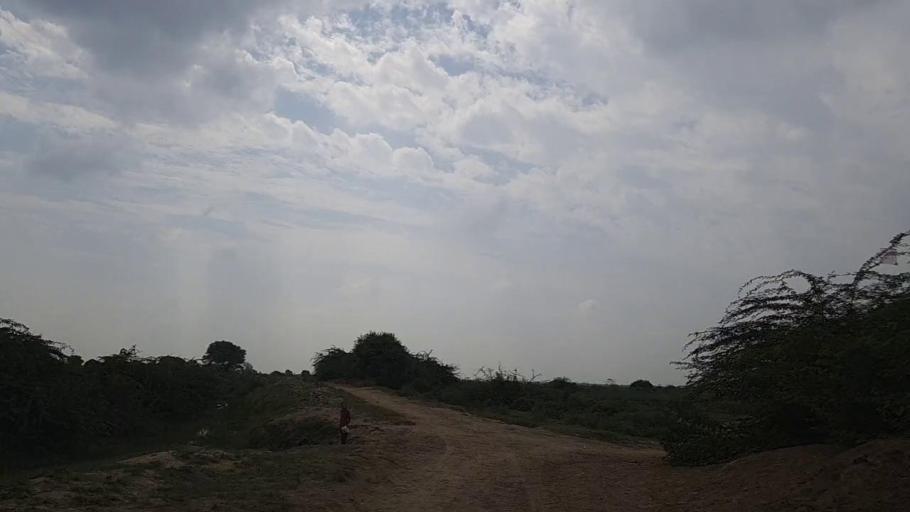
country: PK
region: Sindh
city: Mirpur Batoro
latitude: 24.6195
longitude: 68.1359
